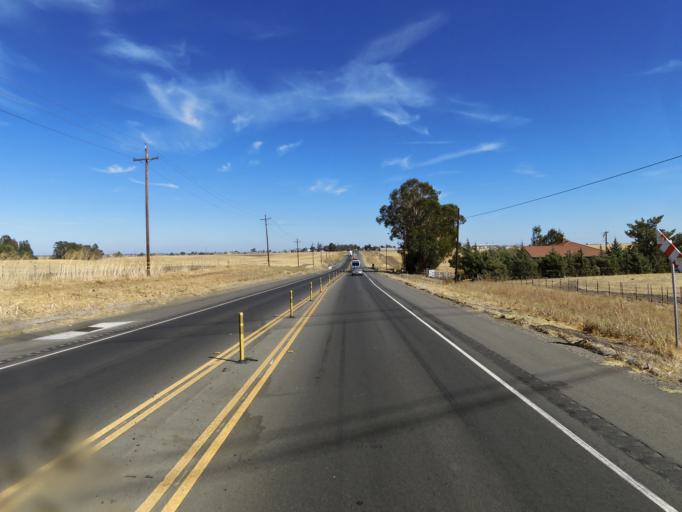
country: US
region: California
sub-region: Solano County
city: Rio Vista
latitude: 38.1834
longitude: -121.7396
